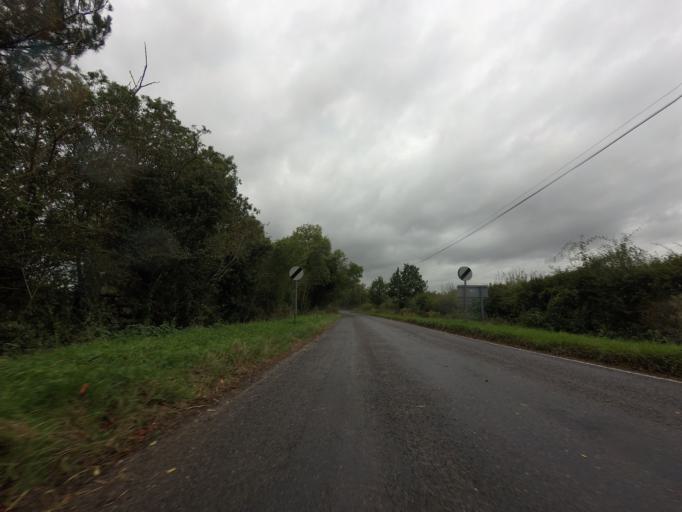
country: GB
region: England
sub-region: Cambridgeshire
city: Comberton
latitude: 52.1689
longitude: -0.0109
